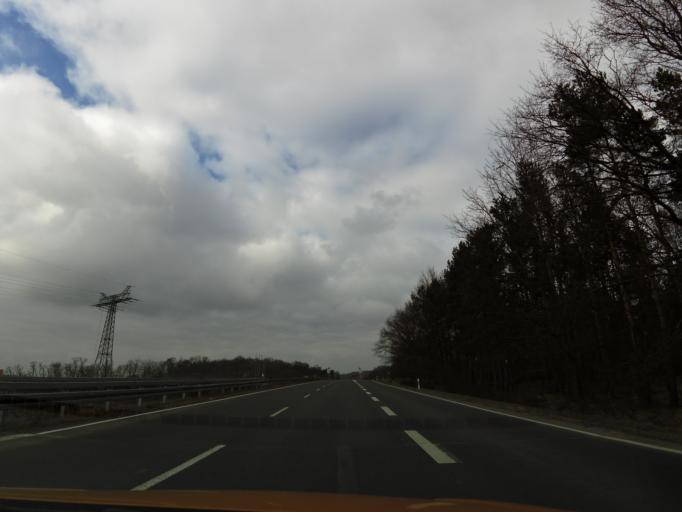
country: DE
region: Brandenburg
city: Wustermark
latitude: 52.4677
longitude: 12.9653
